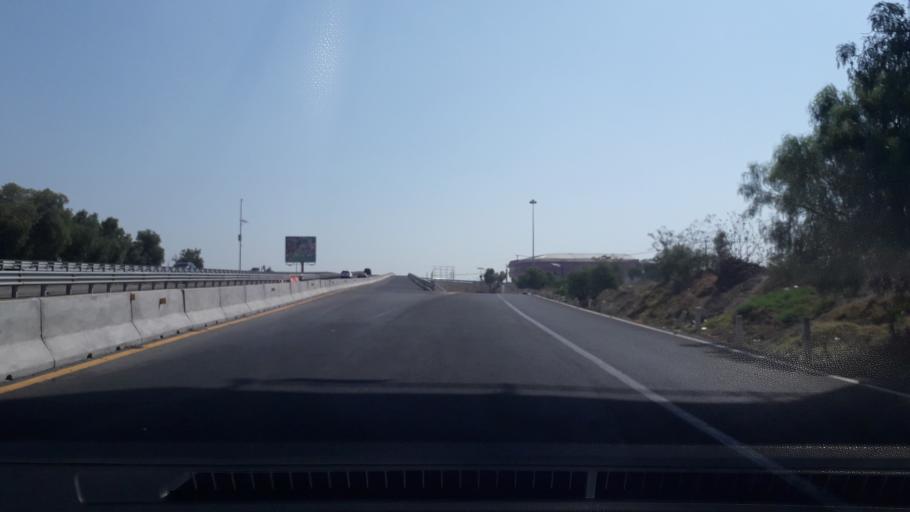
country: MX
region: Mexico
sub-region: Tecamac
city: Ojo de Agua
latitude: 19.6612
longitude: -99.0060
